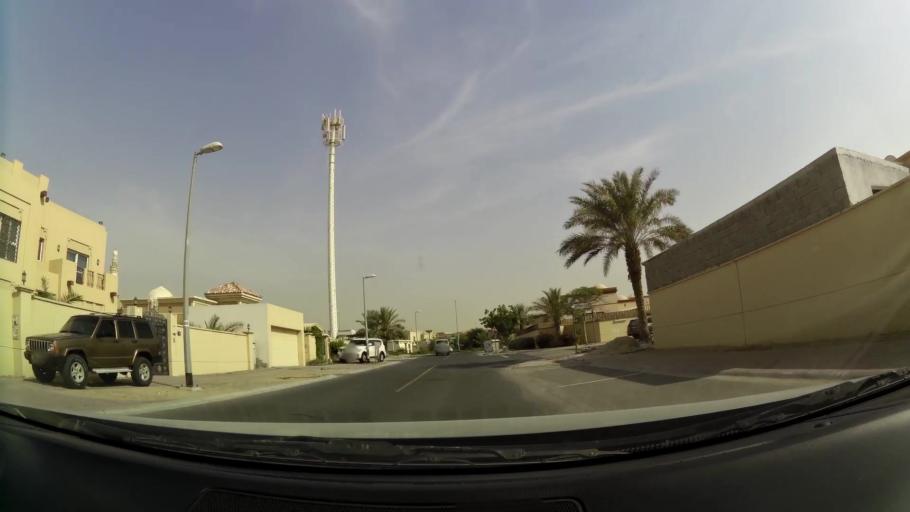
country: AE
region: Ash Shariqah
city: Sharjah
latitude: 25.2703
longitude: 55.4544
